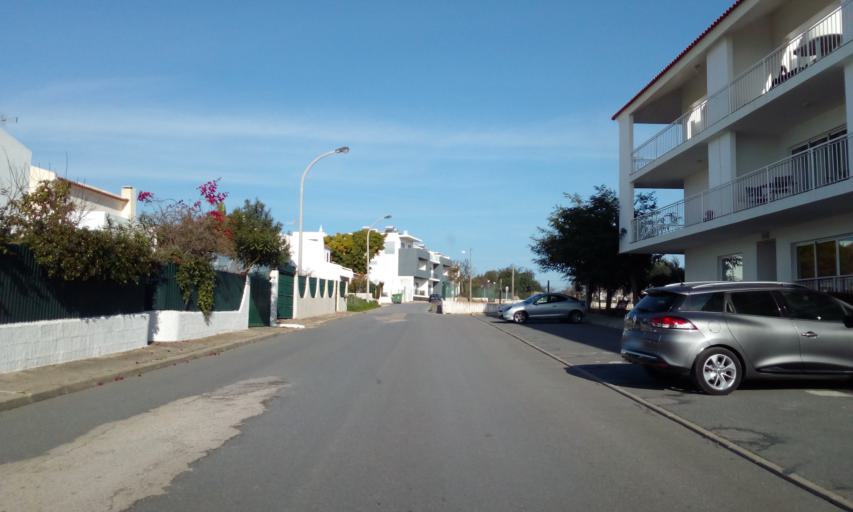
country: PT
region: Faro
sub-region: Tavira
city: Tavira
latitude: 37.1400
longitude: -7.5973
